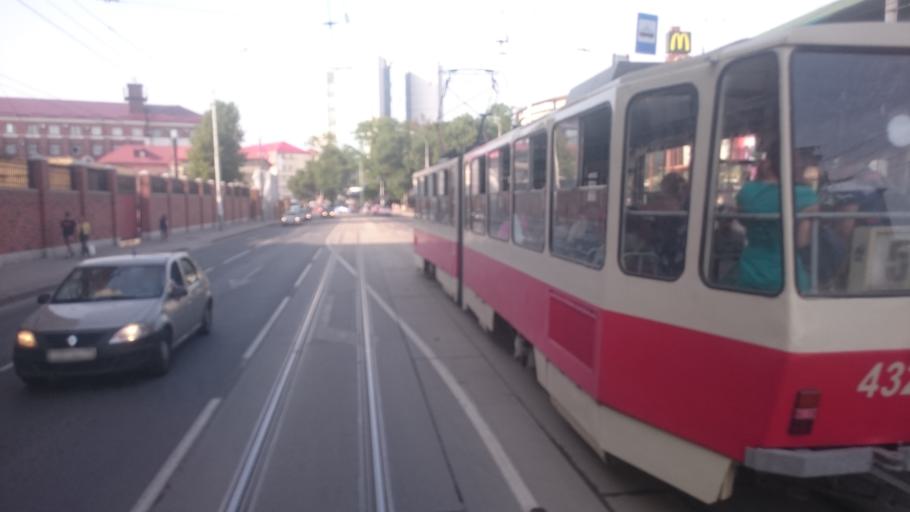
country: RU
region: Kaliningrad
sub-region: Gorod Kaliningrad
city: Kaliningrad
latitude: 54.7217
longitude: 20.4989
